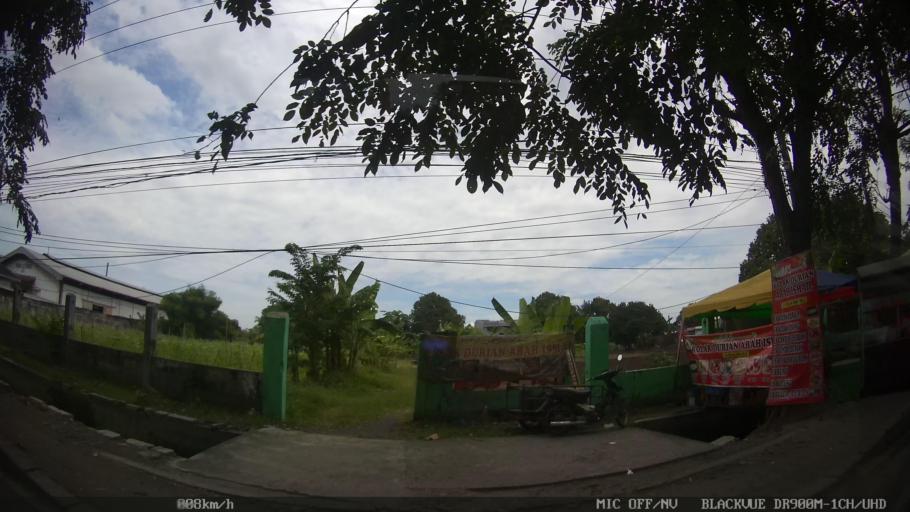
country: ID
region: North Sumatra
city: Sunggal
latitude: 3.5993
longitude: 98.5959
